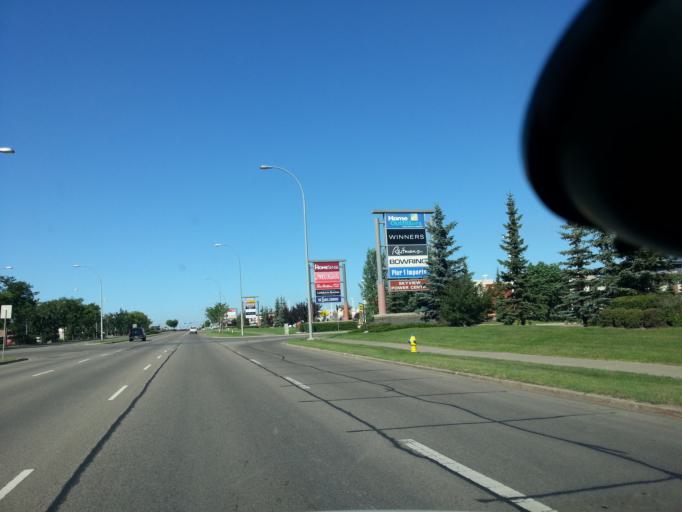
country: CA
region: Alberta
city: St. Albert
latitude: 53.5996
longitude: -113.5554
